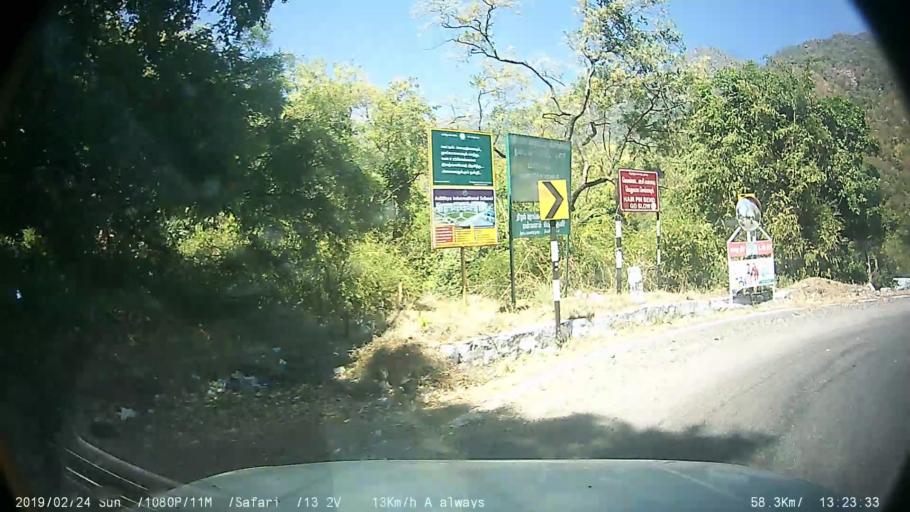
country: IN
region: Tamil Nadu
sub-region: Coimbatore
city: Mettupalayam
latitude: 11.3451
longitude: 76.8745
